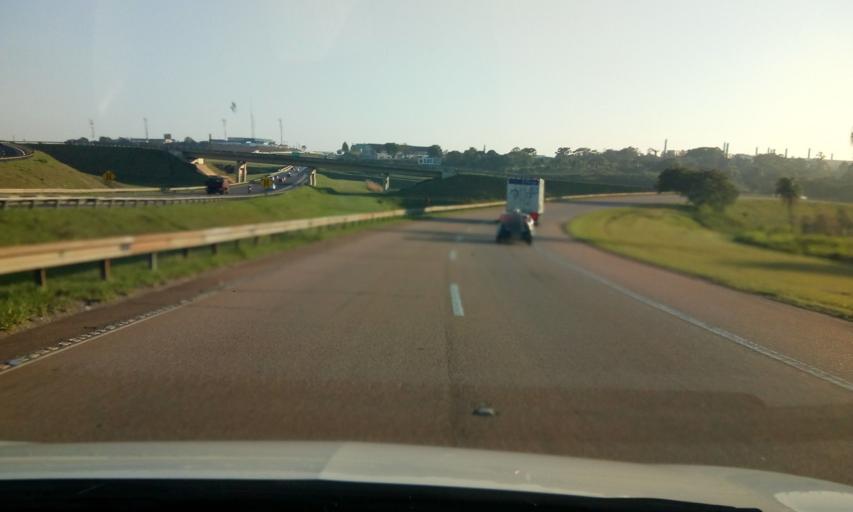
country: BR
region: Sao Paulo
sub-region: Campinas
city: Campinas
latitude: -22.9977
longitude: -47.1097
